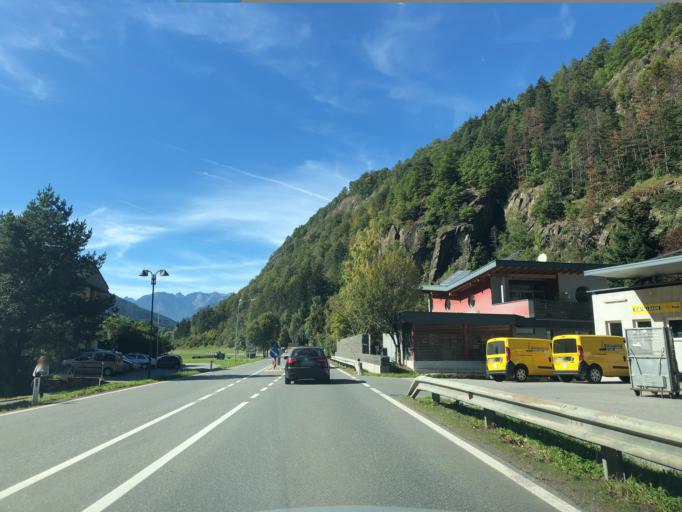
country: AT
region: Tyrol
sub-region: Politischer Bezirk Imst
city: Oetz
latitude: 47.2061
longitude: 10.8857
